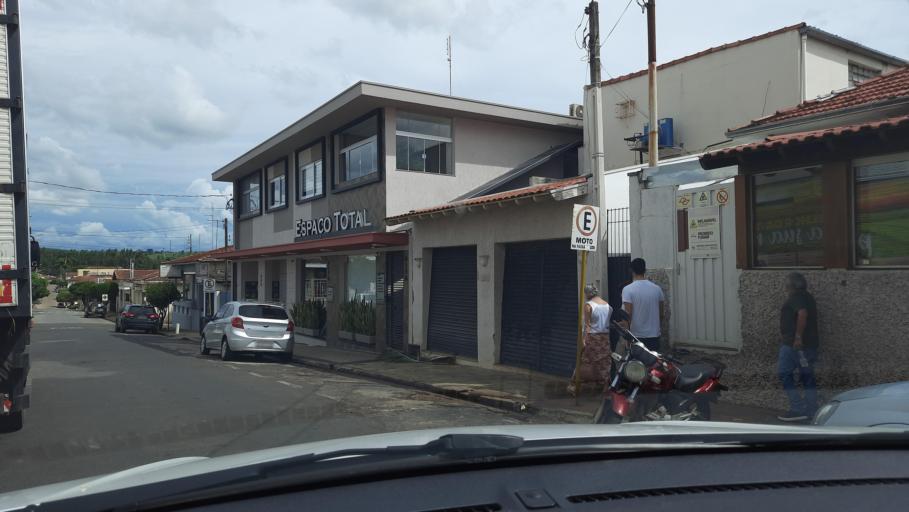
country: BR
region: Sao Paulo
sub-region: Vargem Grande Do Sul
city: Vargem Grande do Sul
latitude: -21.8325
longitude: -46.8924
